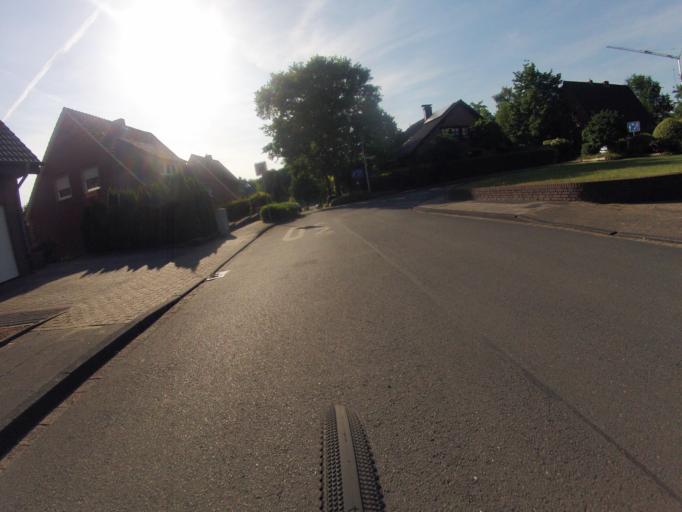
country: DE
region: North Rhine-Westphalia
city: Ibbenburen
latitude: 52.2919
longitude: 7.7048
